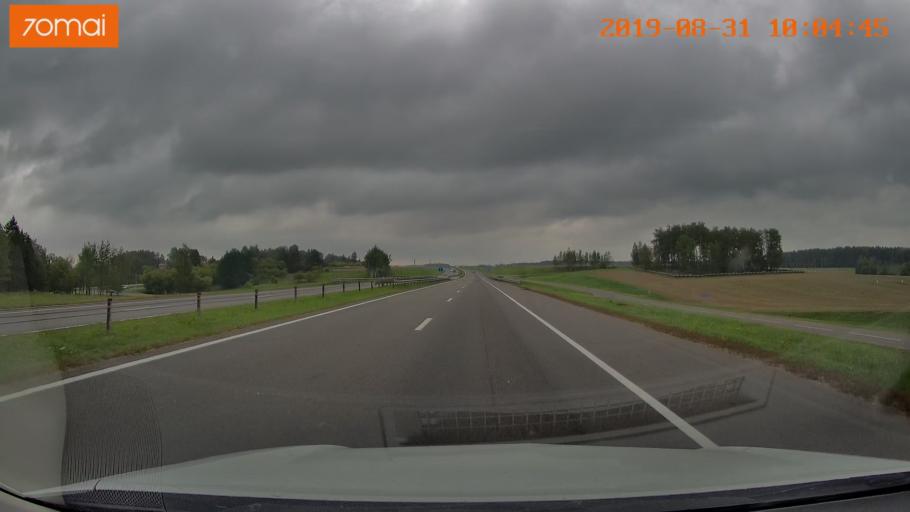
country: BY
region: Mogilev
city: Vishow
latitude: 53.9694
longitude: 30.1521
